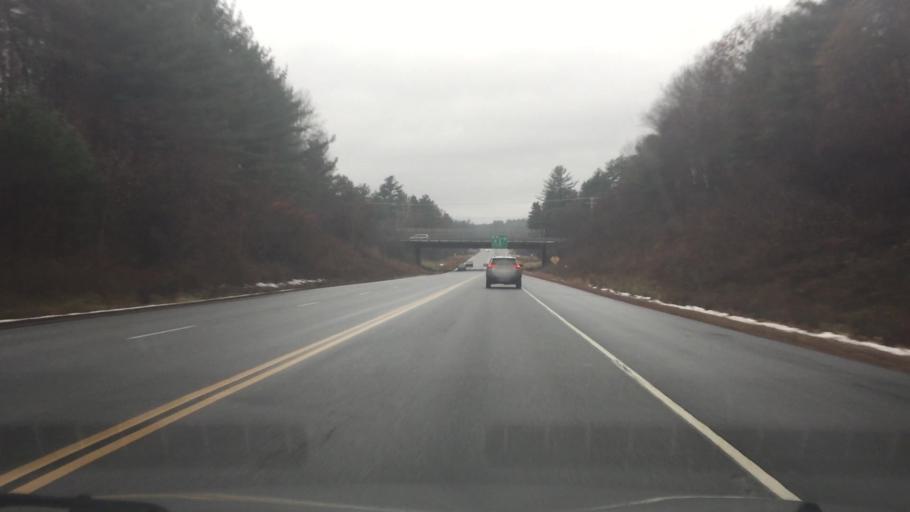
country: US
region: New Hampshire
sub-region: Cheshire County
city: Keene
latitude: 42.9481
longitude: -72.2859
